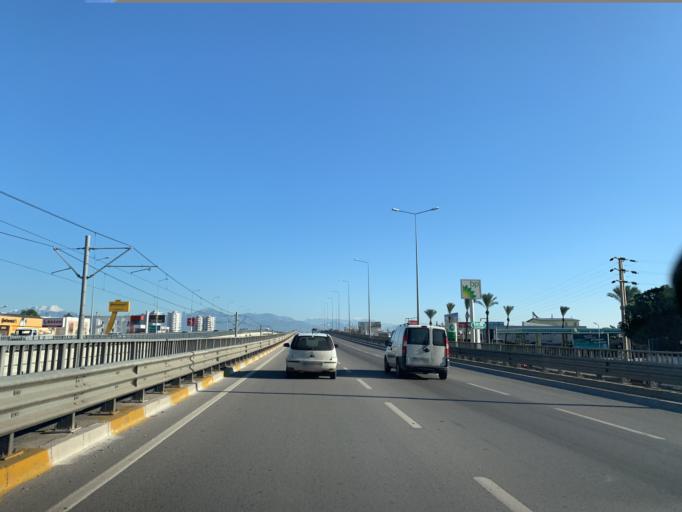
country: TR
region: Antalya
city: Aksu
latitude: 36.9345
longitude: 30.8128
